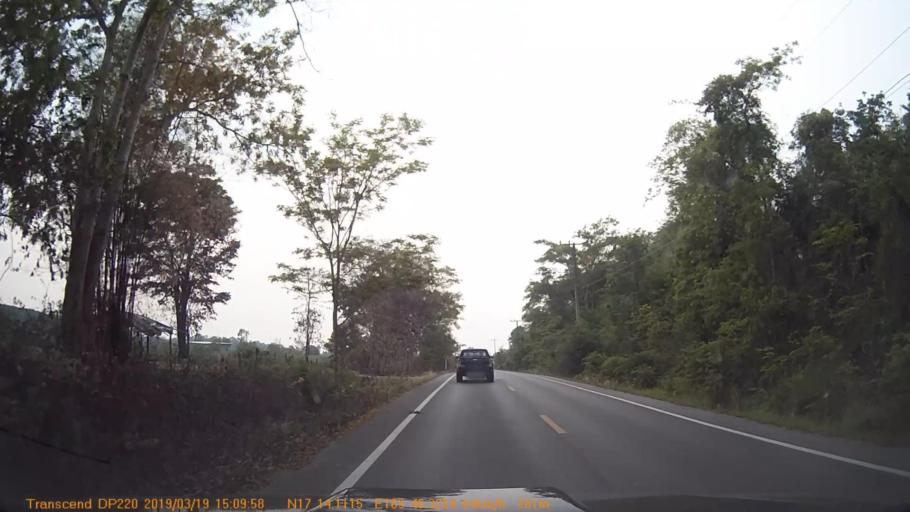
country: TH
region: Sakon Nakhon
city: Nikhom Nam Un
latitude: 17.2353
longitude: 103.7717
